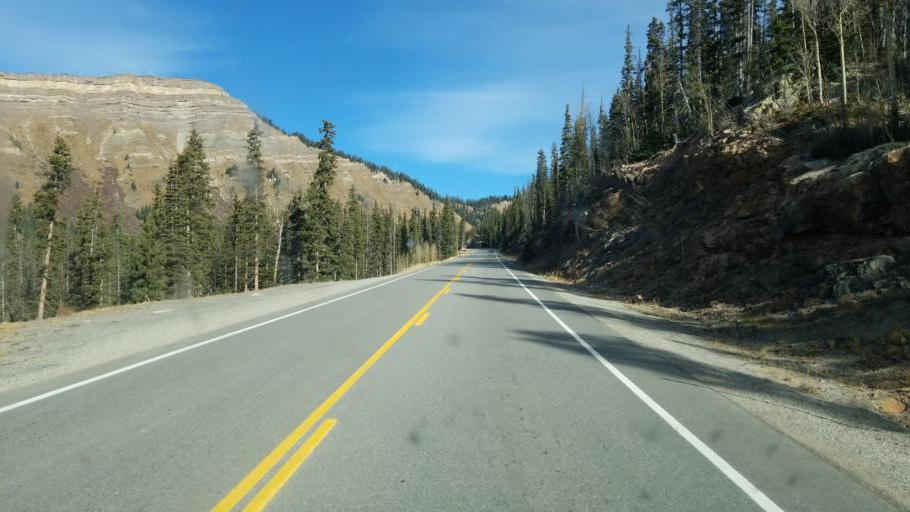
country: US
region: Colorado
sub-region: San Juan County
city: Silverton
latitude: 37.6838
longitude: -107.7793
